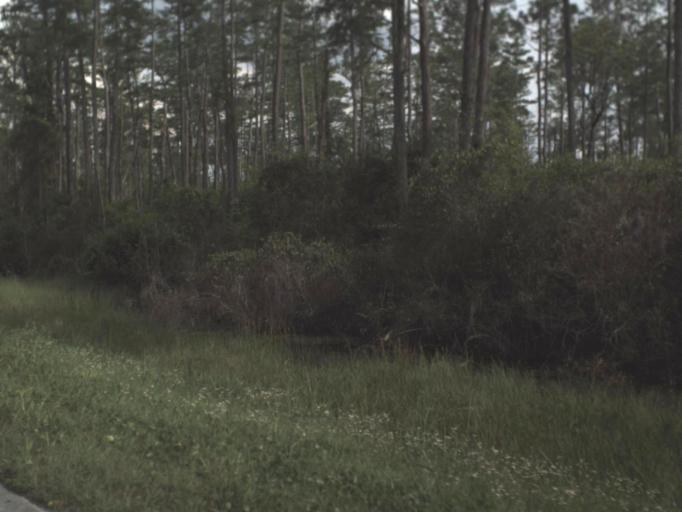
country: US
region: Florida
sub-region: Baker County
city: Macclenny
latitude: 30.5189
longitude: -82.2829
